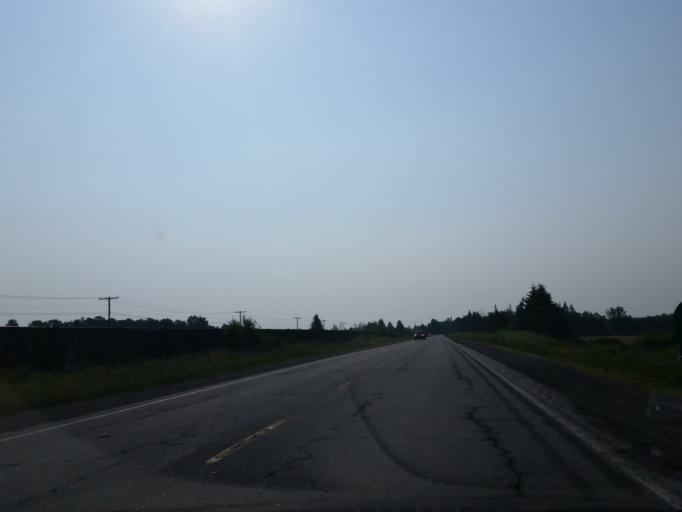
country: CA
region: Ontario
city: Greater Sudbury
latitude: 46.4384
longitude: -80.2908
